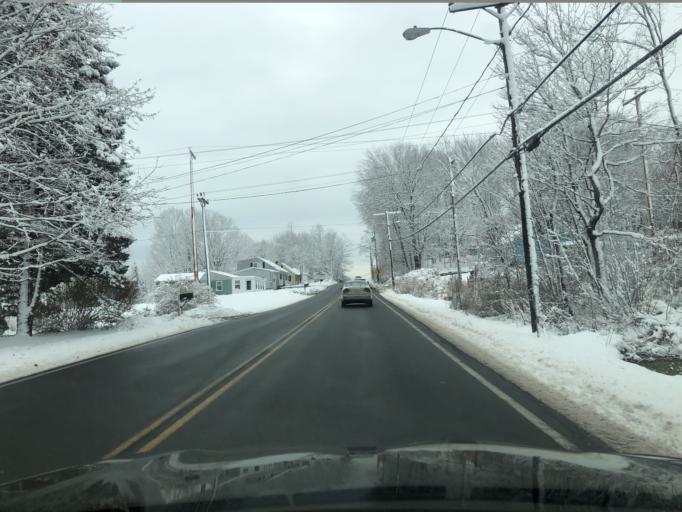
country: US
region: New Hampshire
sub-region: Strafford County
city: Dover
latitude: 43.2105
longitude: -70.8648
